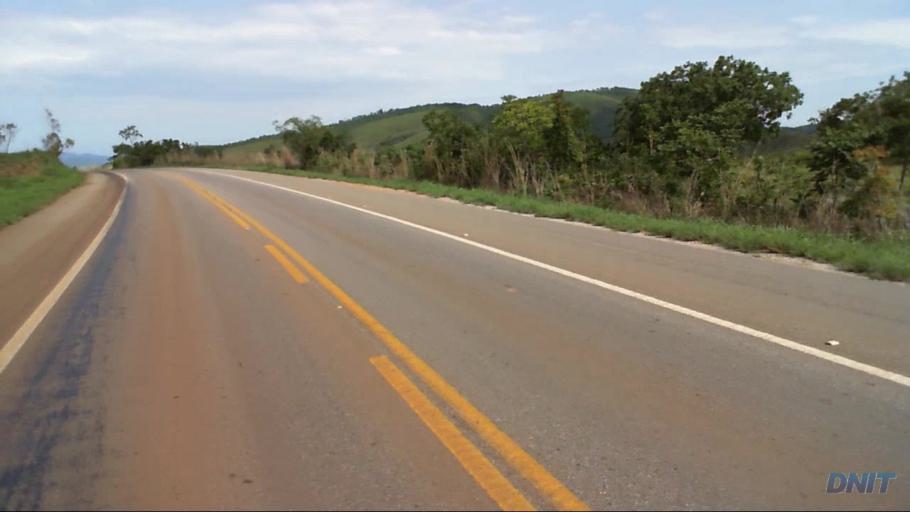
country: BR
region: Goias
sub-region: Barro Alto
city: Barro Alto
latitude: -15.1497
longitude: -48.8096
